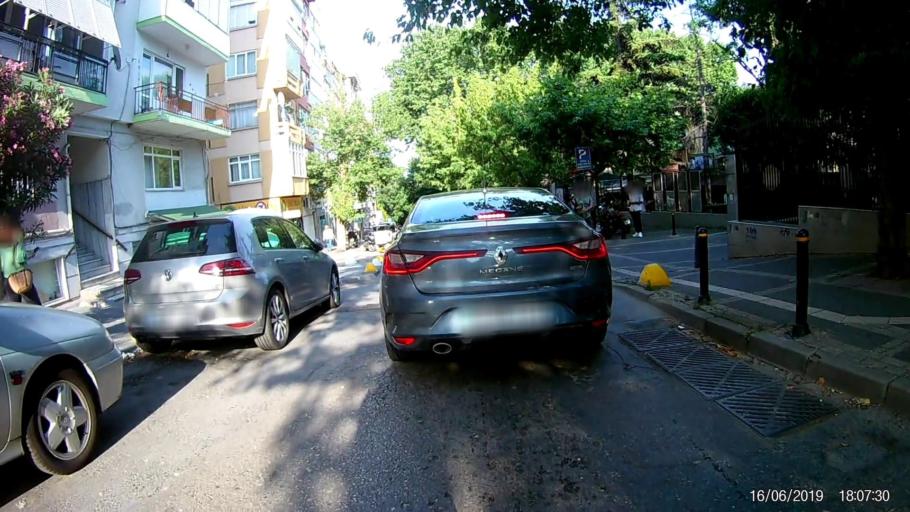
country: TR
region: Istanbul
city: UEskuedar
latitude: 40.9834
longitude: 29.0295
